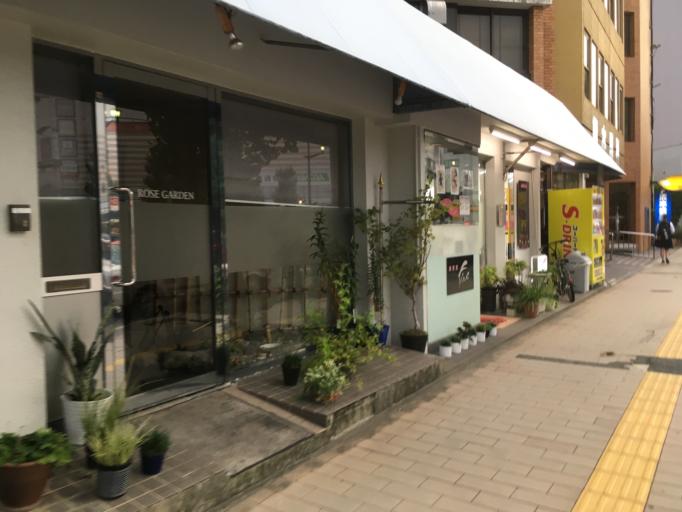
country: JP
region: Kumamoto
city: Kumamoto
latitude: 32.7988
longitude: 130.7185
